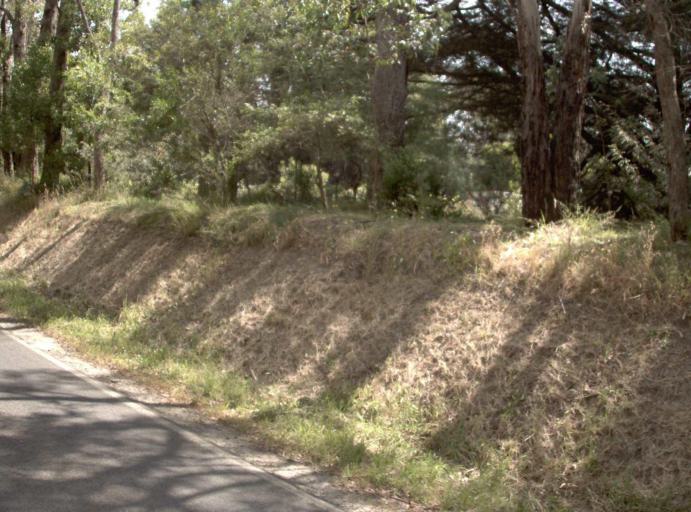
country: AU
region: Victoria
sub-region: Latrobe
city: Traralgon
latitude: -38.2925
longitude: 146.5391
